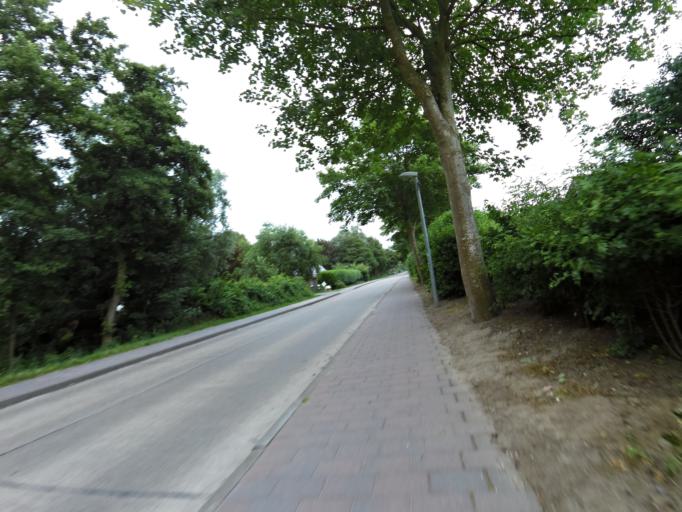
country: DE
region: Lower Saxony
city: Padingbuttel
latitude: 53.7354
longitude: 8.5213
